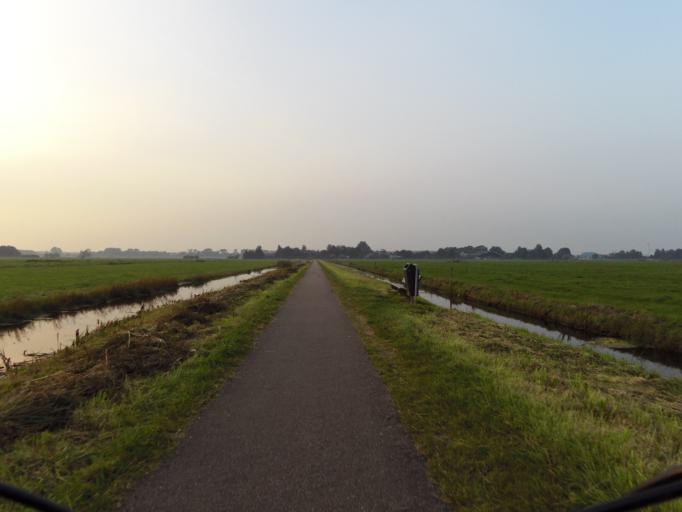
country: NL
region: South Holland
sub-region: Gemeente Voorschoten
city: Voorschoten
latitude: 52.1059
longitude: 4.4825
